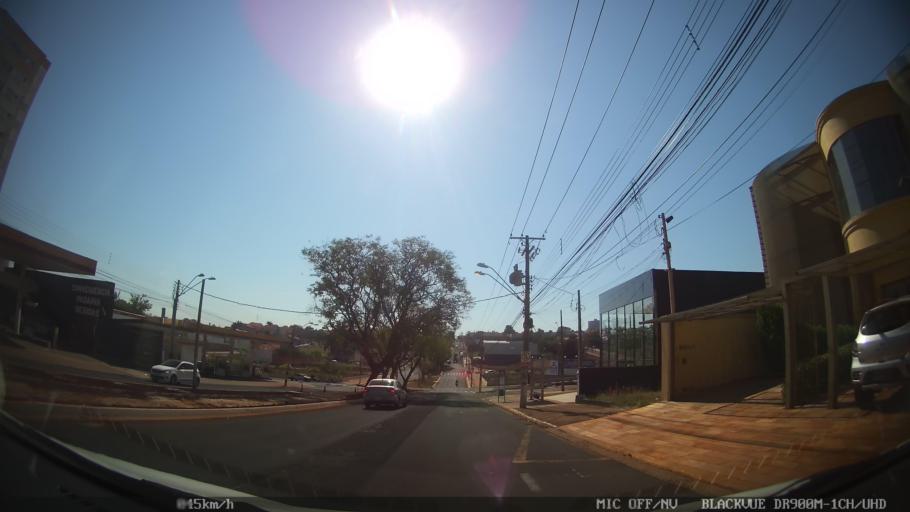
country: BR
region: Sao Paulo
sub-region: Ribeirao Preto
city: Ribeirao Preto
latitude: -21.2048
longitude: -47.8208
